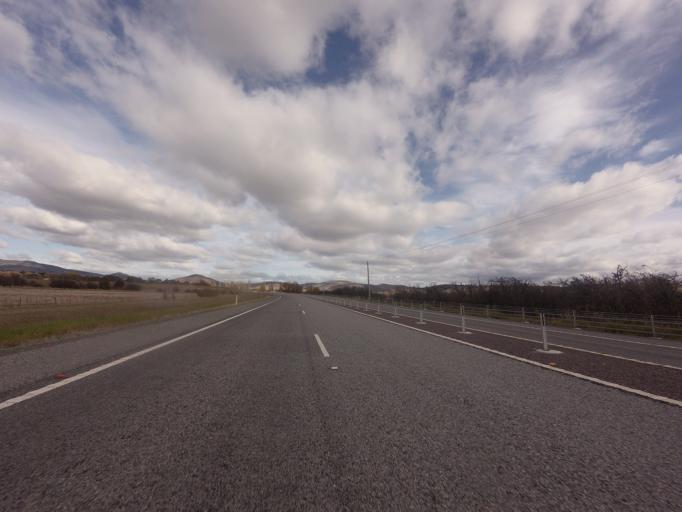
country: AU
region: Tasmania
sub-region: Brighton
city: Bridgewater
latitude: -42.4785
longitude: 147.1801
